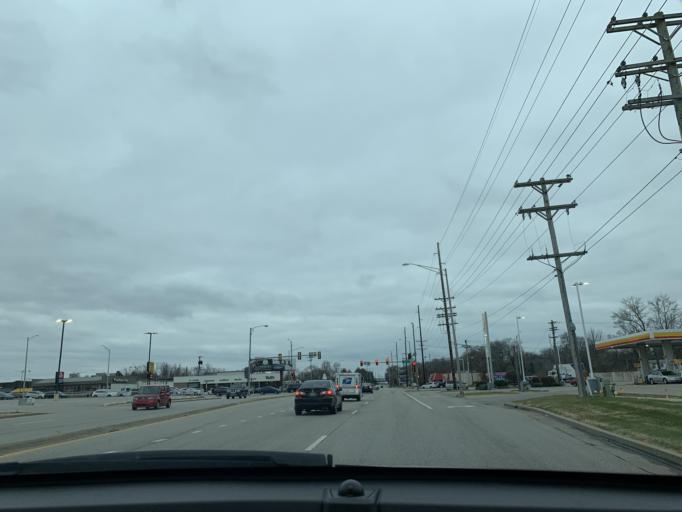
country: US
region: Illinois
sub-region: Sangamon County
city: Jerome
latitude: 39.7652
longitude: -89.6870
